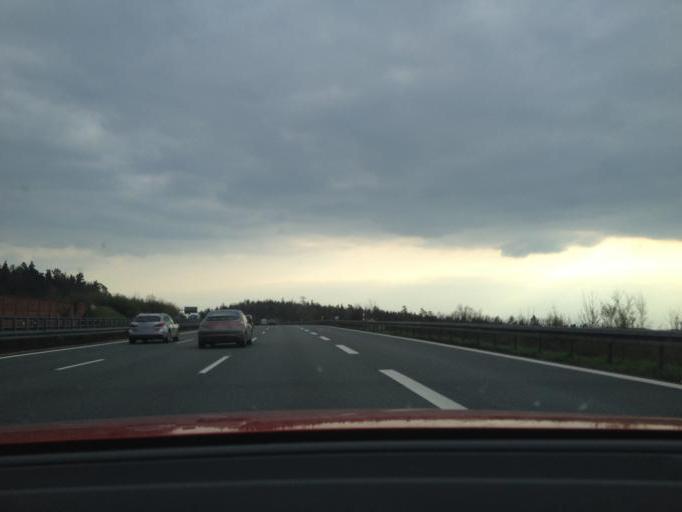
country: DE
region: Bavaria
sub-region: Regierungsbezirk Mittelfranken
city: Schnaittach
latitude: 49.5654
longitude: 11.3290
